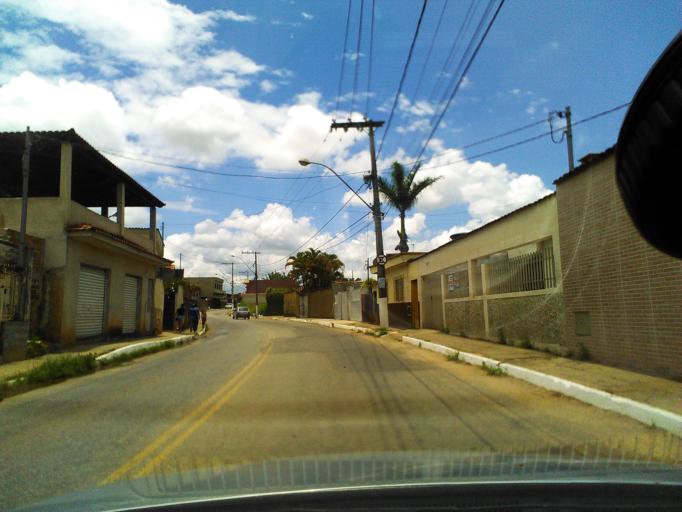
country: BR
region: Minas Gerais
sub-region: Tres Coracoes
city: Tres Coracoes
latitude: -21.7169
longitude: -45.2626
